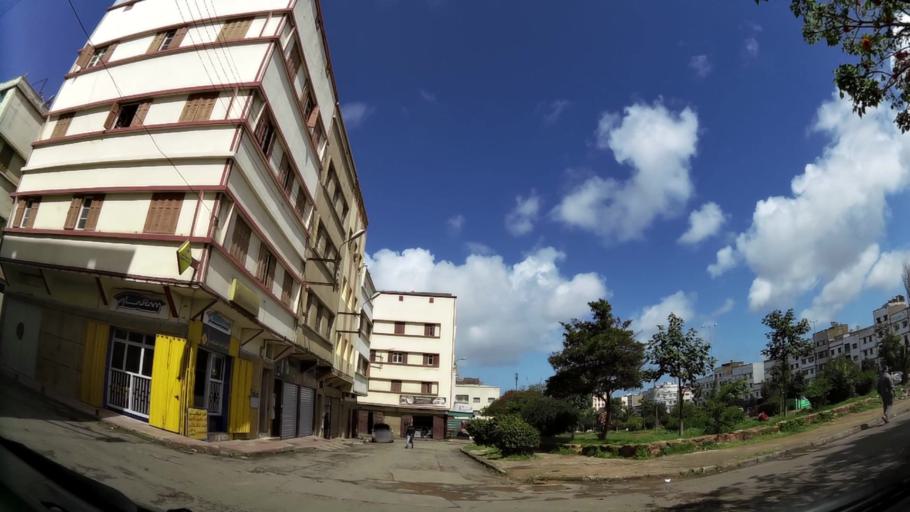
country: MA
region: Grand Casablanca
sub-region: Casablanca
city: Casablanca
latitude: 33.5416
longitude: -7.5809
